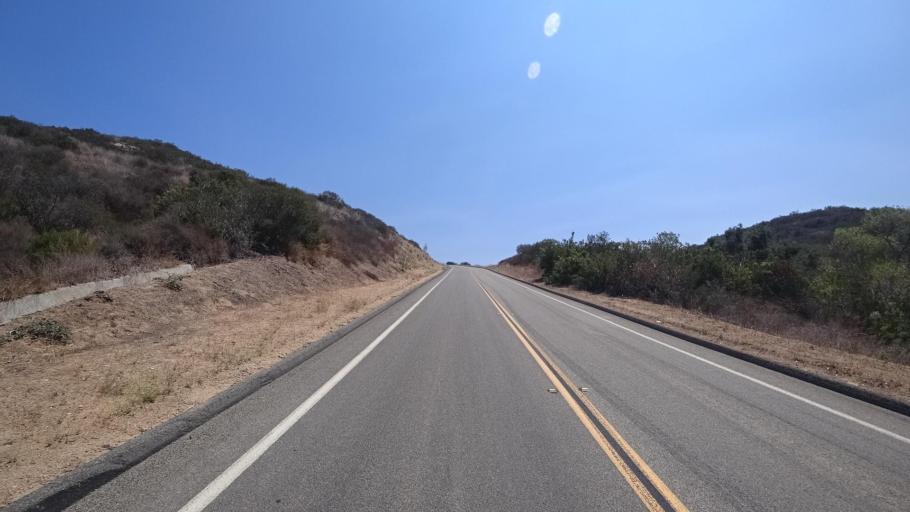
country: US
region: California
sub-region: San Diego County
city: Bonsall
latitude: 33.2748
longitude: -117.2266
